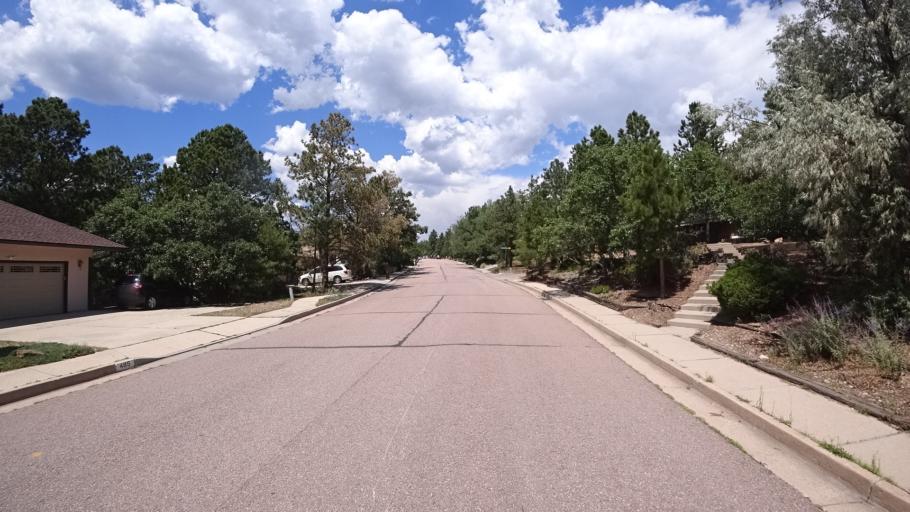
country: US
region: Colorado
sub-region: El Paso County
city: Air Force Academy
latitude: 38.9378
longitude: -104.8366
